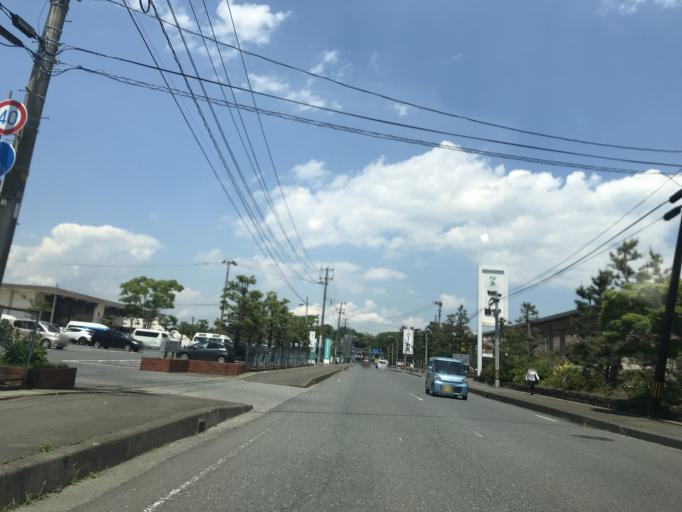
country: JP
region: Miyagi
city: Matsushima
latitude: 38.3775
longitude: 141.0709
